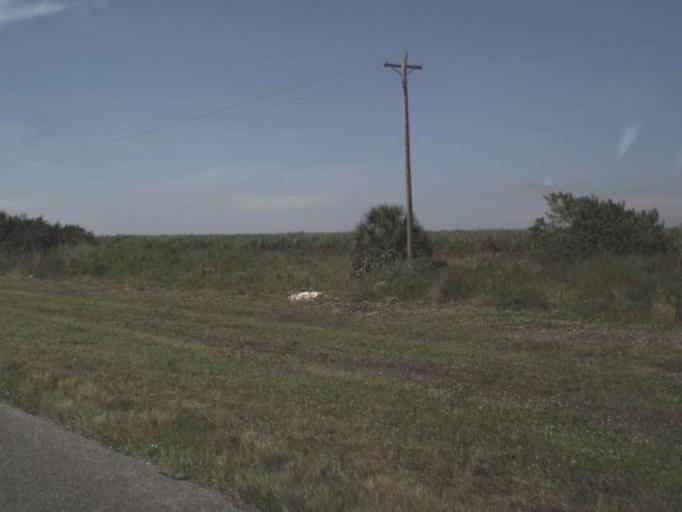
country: US
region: Florida
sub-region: Glades County
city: Moore Haven
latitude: 26.8339
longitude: -81.1685
